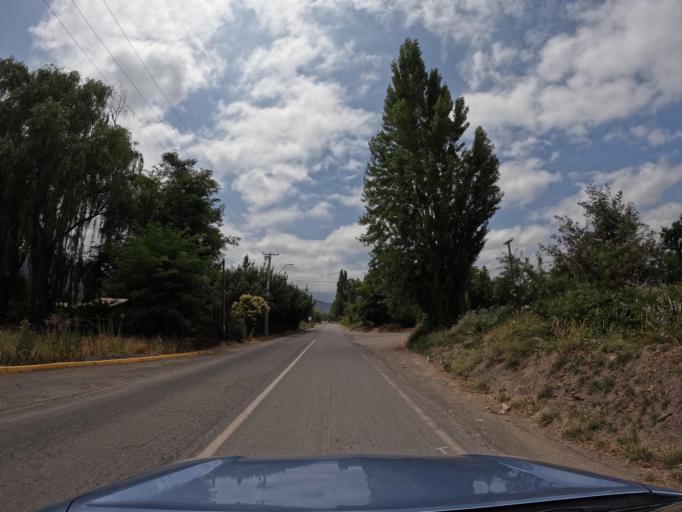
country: CL
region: O'Higgins
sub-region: Provincia de Colchagua
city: Chimbarongo
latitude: -34.7451
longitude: -70.9644
